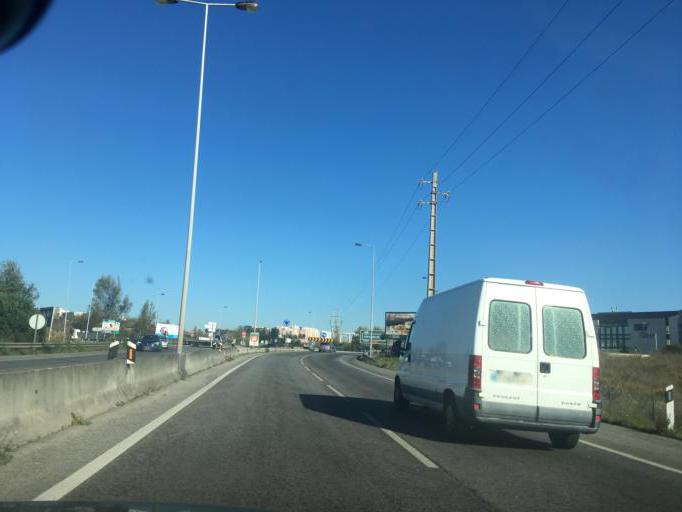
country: PT
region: Lisbon
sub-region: Oeiras
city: Porto Salvo
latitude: 38.7348
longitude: -9.2982
